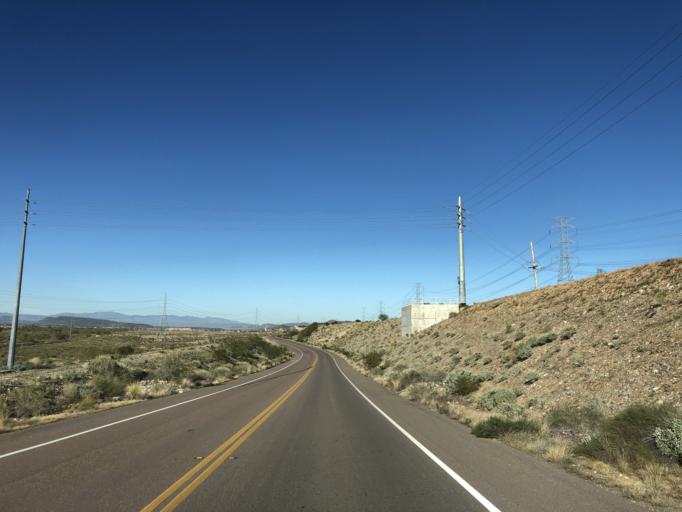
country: US
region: Arizona
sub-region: Maricopa County
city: Sun City West
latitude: 33.6806
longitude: -112.2984
